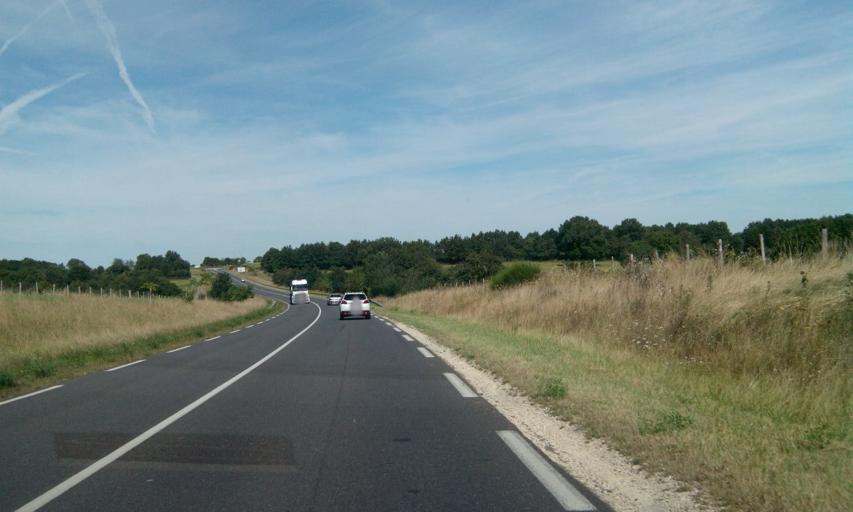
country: FR
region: Poitou-Charentes
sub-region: Departement de la Vienne
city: Charroux
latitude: 46.1472
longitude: 0.4136
